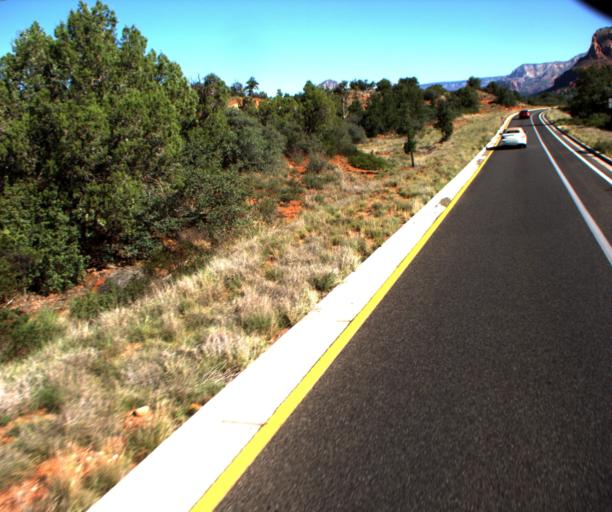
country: US
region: Arizona
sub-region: Yavapai County
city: Village of Oak Creek (Big Park)
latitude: 34.8054
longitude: -111.7676
